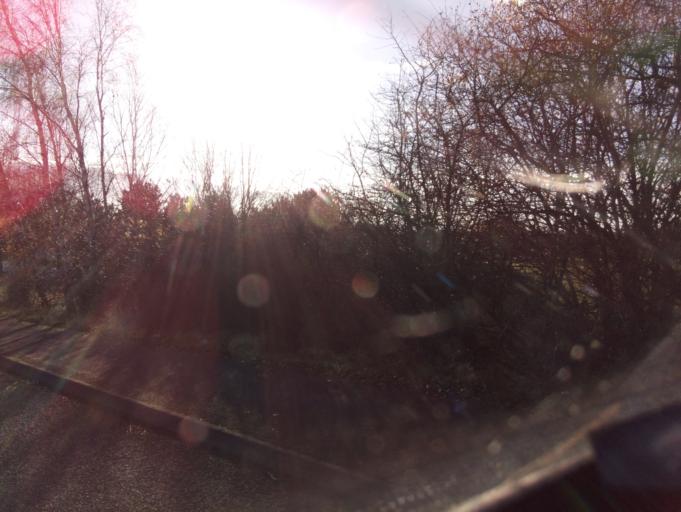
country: GB
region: England
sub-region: Derbyshire
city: Etwall
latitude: 52.8721
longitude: -1.6008
